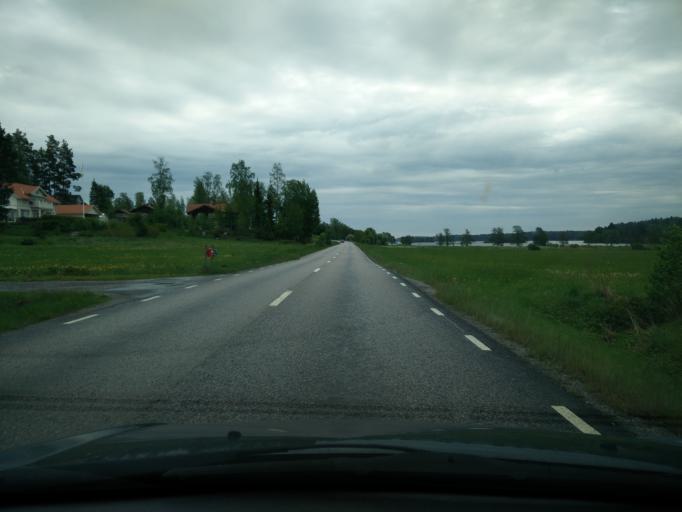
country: SE
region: Stockholm
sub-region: Norrtalje Kommun
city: Norrtalje
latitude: 59.7794
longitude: 18.8137
